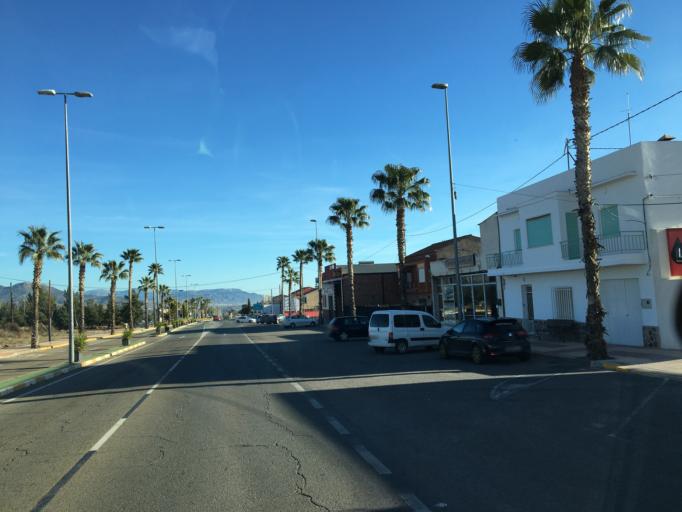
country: ES
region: Murcia
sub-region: Murcia
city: Puerto Lumbreras
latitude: 37.5722
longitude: -1.7983
